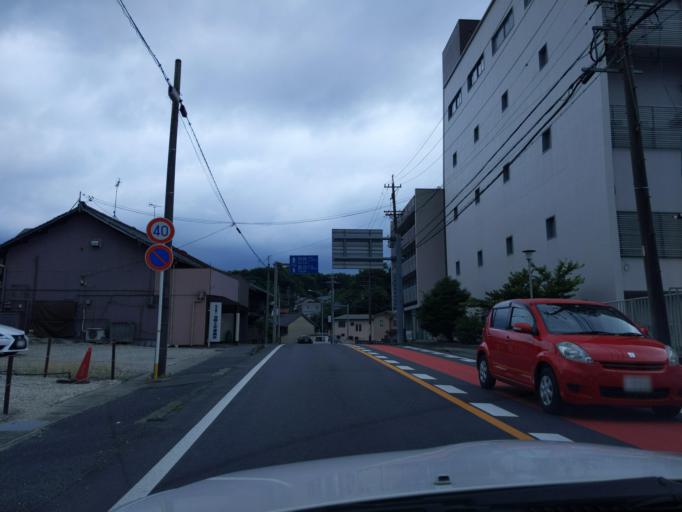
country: JP
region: Aichi
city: Seto
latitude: 35.2237
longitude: 137.1011
